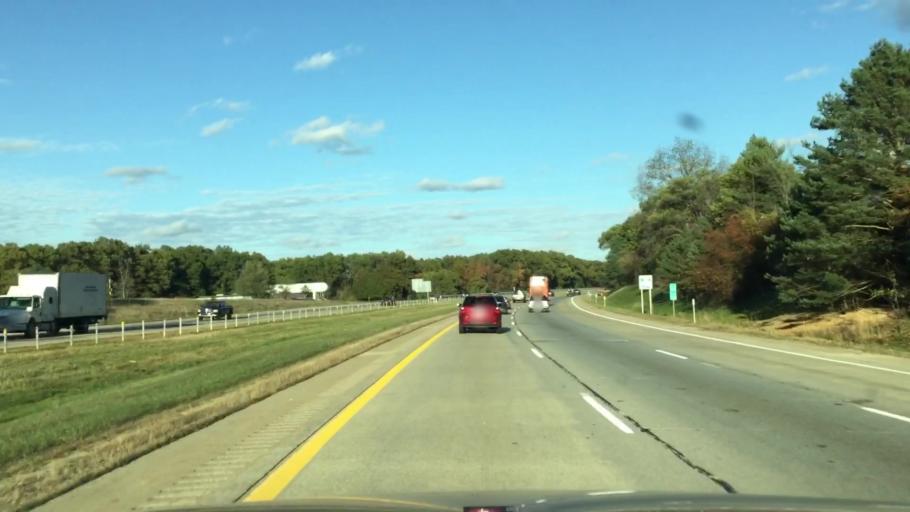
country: US
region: Michigan
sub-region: Calhoun County
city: Brownlee Park
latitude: 42.2830
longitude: -85.1531
